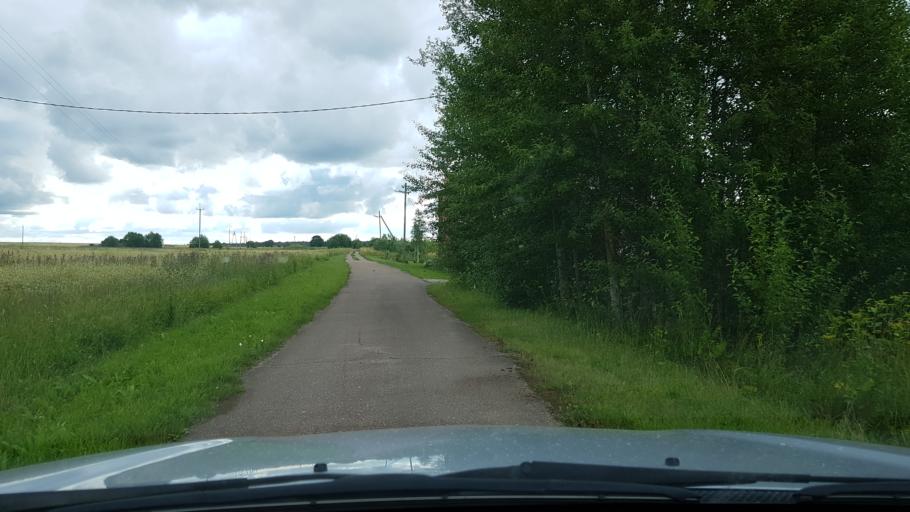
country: EE
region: Ida-Virumaa
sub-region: Narva-Joesuu linn
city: Narva-Joesuu
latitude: 59.3883
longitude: 27.9849
